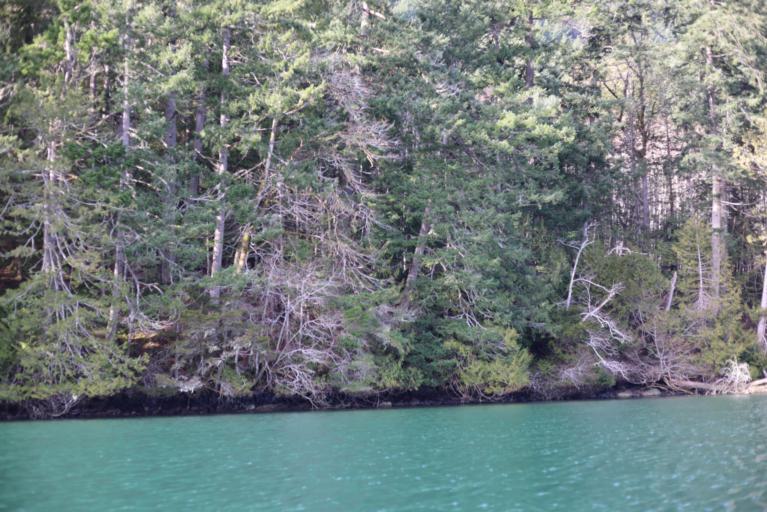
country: CA
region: British Columbia
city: Duncan
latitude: 48.7665
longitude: -123.5990
